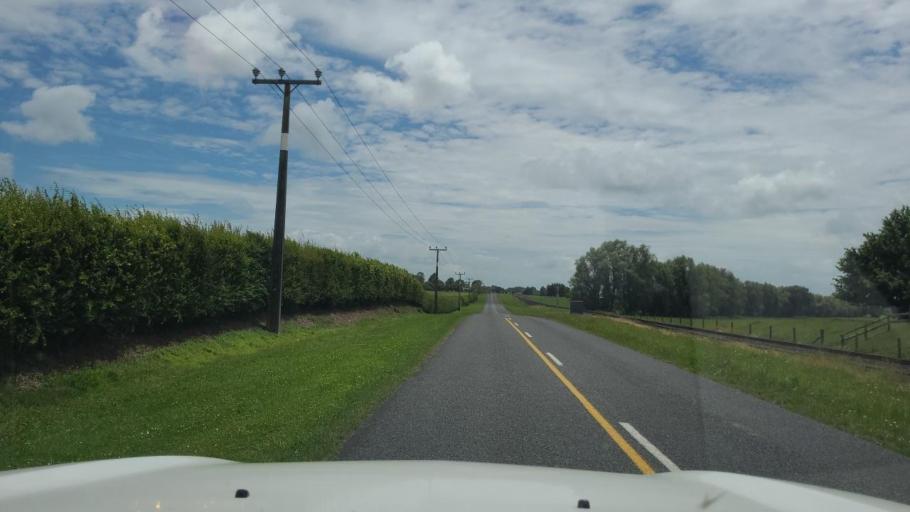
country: NZ
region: Waikato
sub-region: Matamata-Piako District
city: Matamata
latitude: -37.8741
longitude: 175.7574
